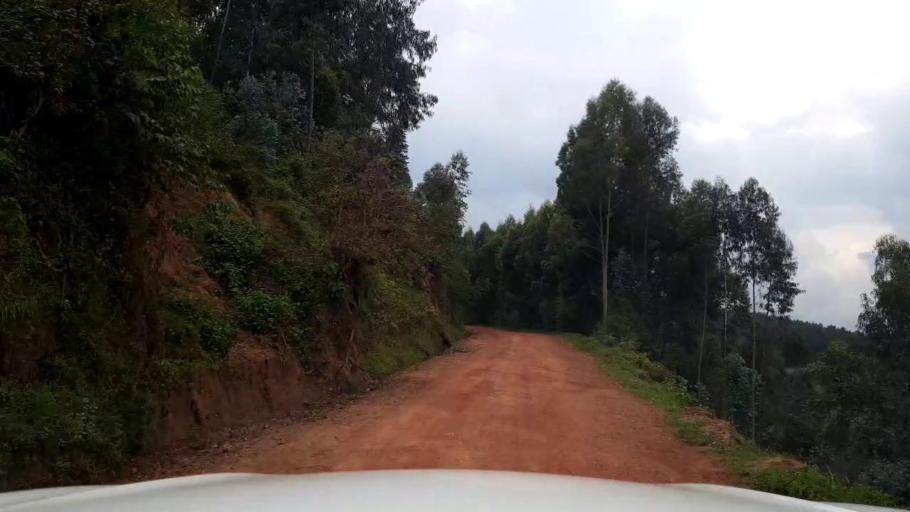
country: RW
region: Northern Province
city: Byumba
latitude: -1.5045
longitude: 29.9352
